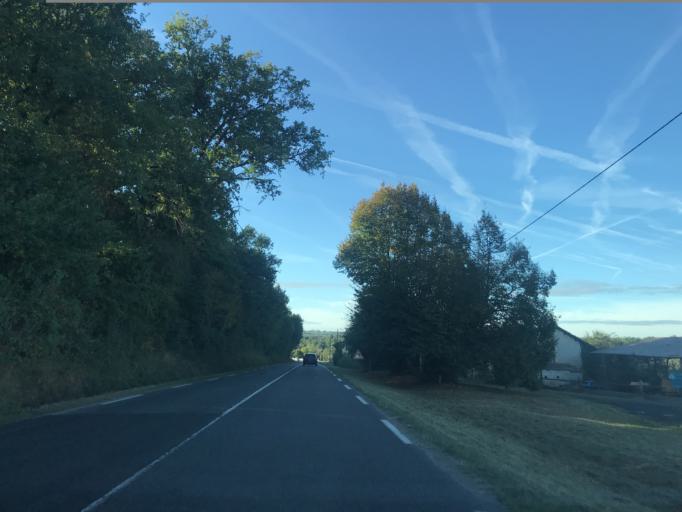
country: FR
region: Poitou-Charentes
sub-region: Departement de la Charente-Maritime
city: Montguyon
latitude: 45.2013
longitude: -0.1471
